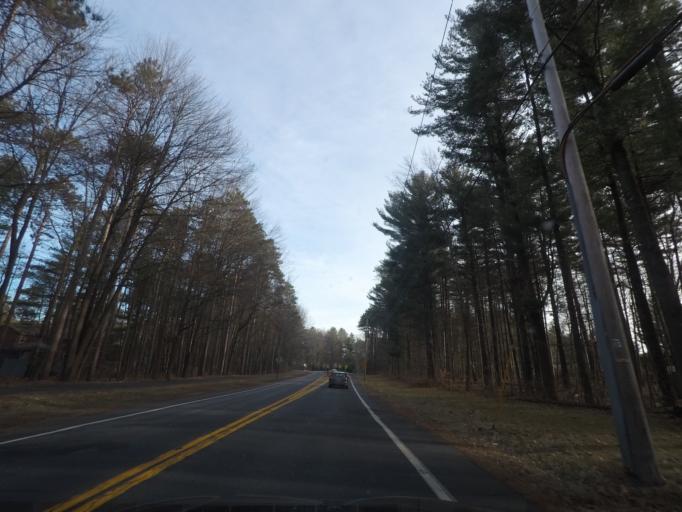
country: US
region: New York
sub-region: Saratoga County
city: Country Knolls
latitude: 42.9724
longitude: -73.7780
